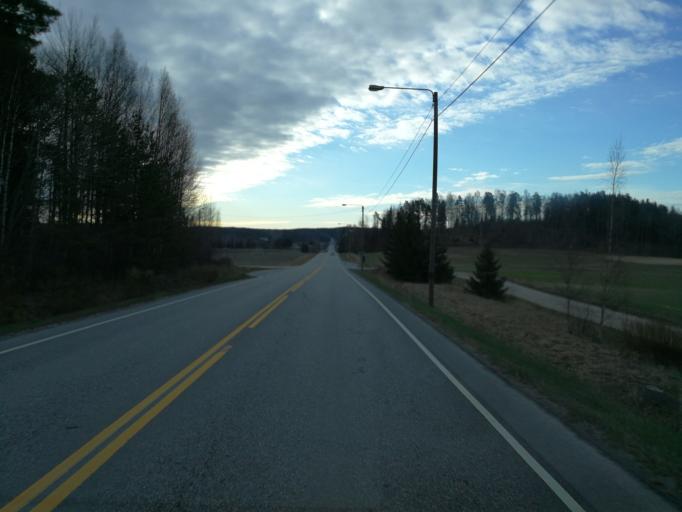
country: FI
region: Varsinais-Suomi
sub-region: Turku
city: Paimio
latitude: 60.4242
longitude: 22.6376
